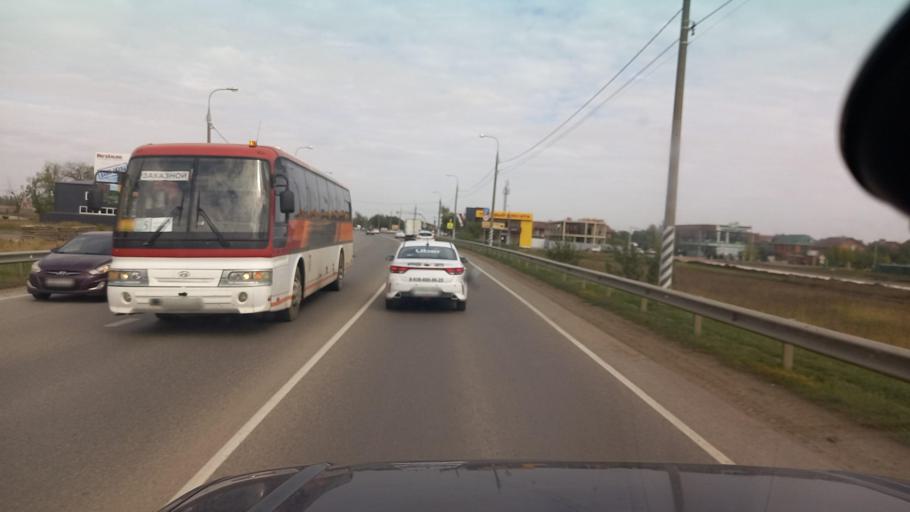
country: RU
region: Krasnodarskiy
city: Krasnodar
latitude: 45.1015
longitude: 38.9155
